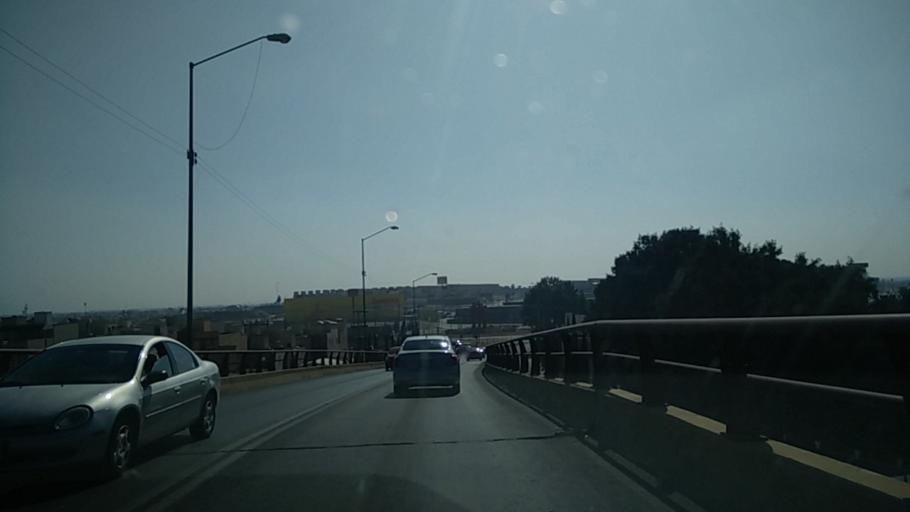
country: MX
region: Mexico
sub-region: Atenco
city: Colonia el Salado
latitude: 19.5873
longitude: -99.0238
